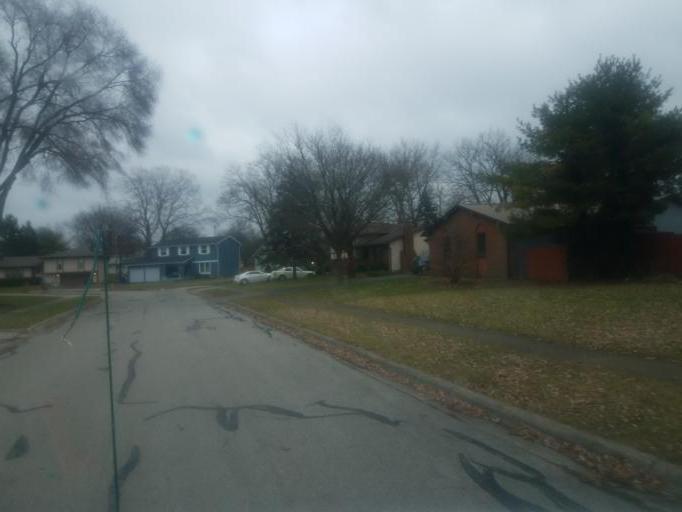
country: US
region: Ohio
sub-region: Franklin County
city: Minerva Park
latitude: 40.0777
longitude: -82.9726
